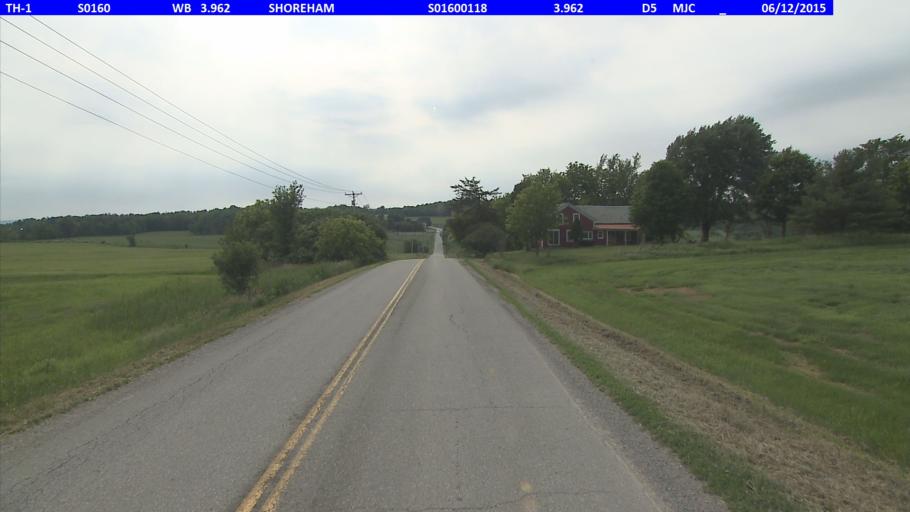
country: US
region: Vermont
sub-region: Addison County
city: Middlebury (village)
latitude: 43.8696
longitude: -73.2399
